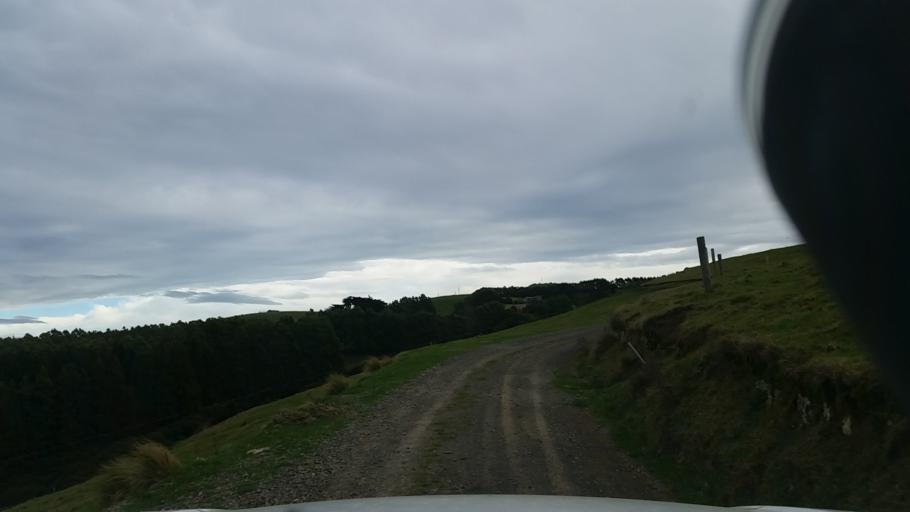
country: NZ
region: Canterbury
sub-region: Christchurch City
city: Christchurch
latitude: -43.8615
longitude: 173.0292
